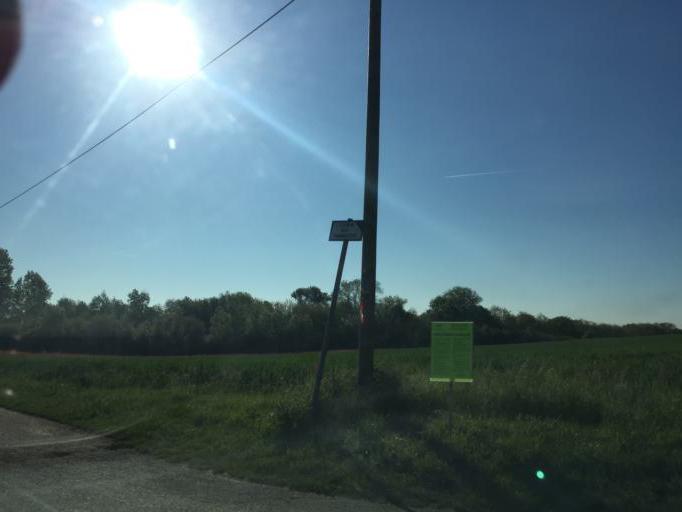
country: FR
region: Rhone-Alpes
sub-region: Departement de l'Ain
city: Beynost
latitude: 45.8474
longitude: 4.9938
